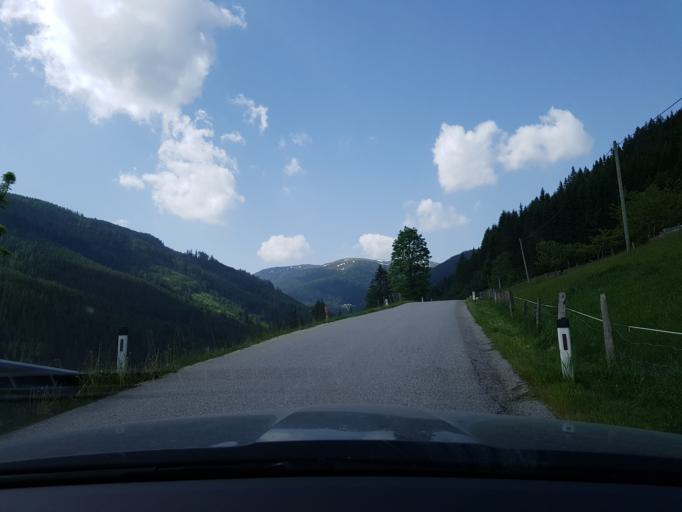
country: AT
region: Salzburg
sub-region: Politischer Bezirk Tamsweg
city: Thomatal
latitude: 47.0642
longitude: 13.7185
